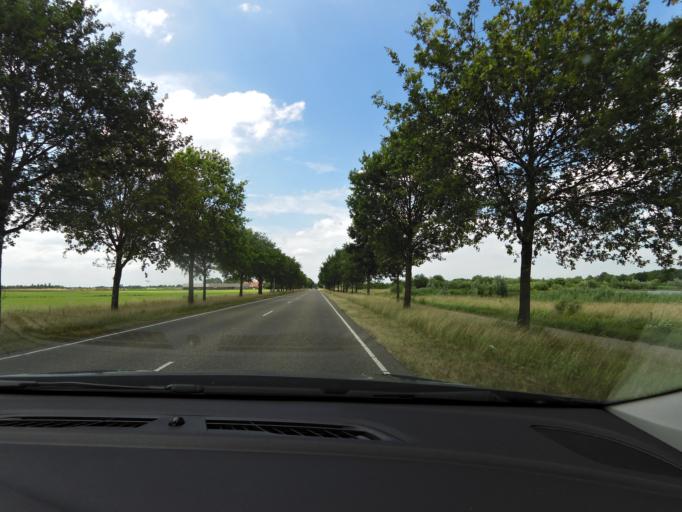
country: NL
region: North Brabant
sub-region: Gemeente Baarle-Nassau
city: Baarle-Nassau
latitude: 51.4840
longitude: 4.8854
